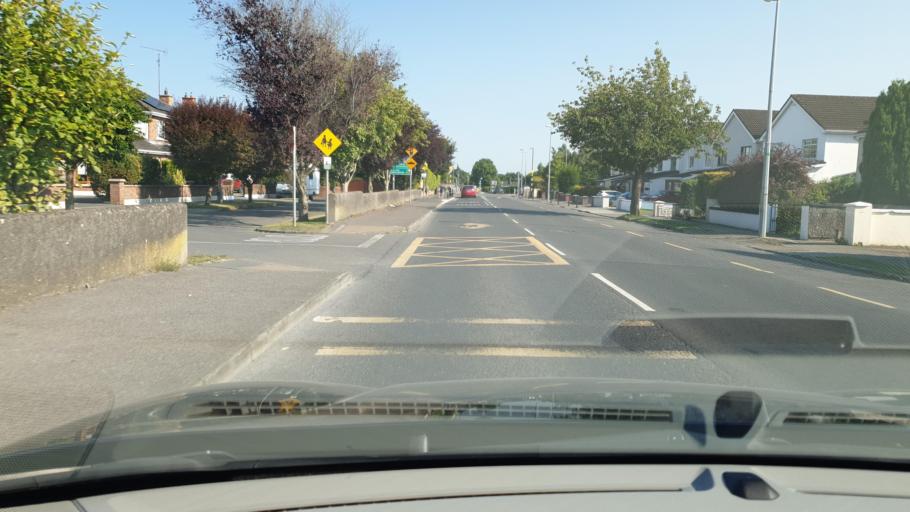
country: IE
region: Leinster
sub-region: An Mhi
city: Navan
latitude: 53.6593
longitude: -6.6868
